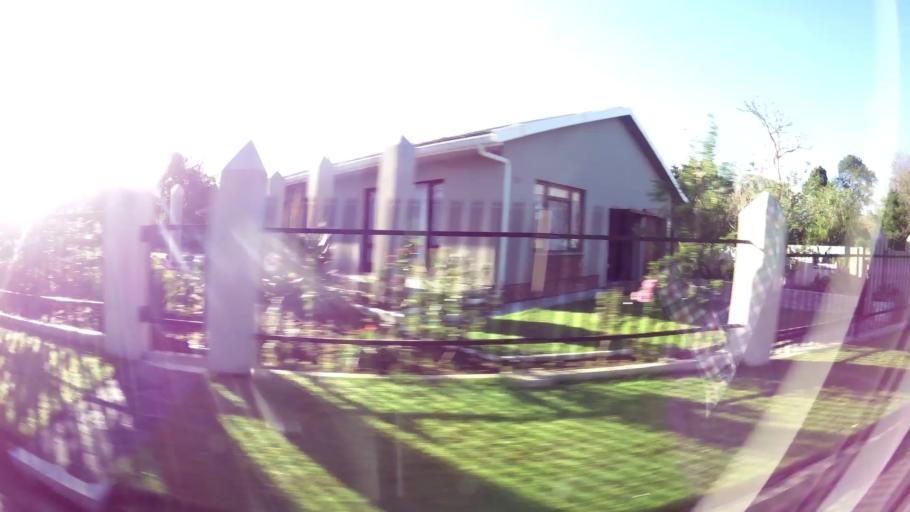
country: ZA
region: Western Cape
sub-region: Eden District Municipality
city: George
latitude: -33.9446
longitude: 22.4566
